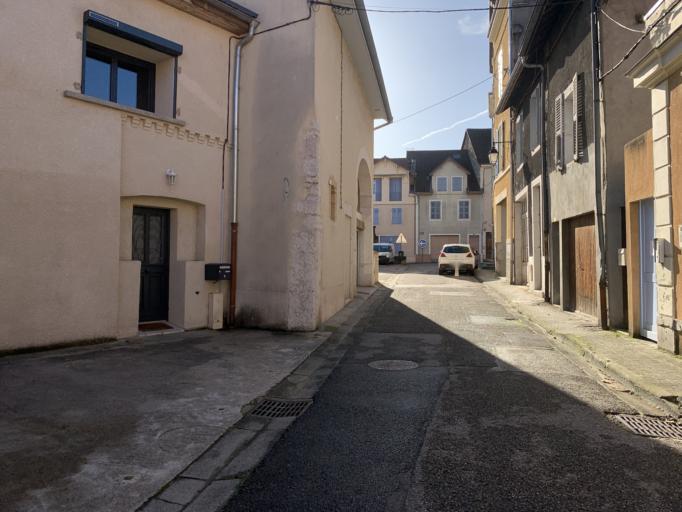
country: FR
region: Rhone-Alpes
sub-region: Departement de l'Ain
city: Belley
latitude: 45.7587
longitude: 5.6870
